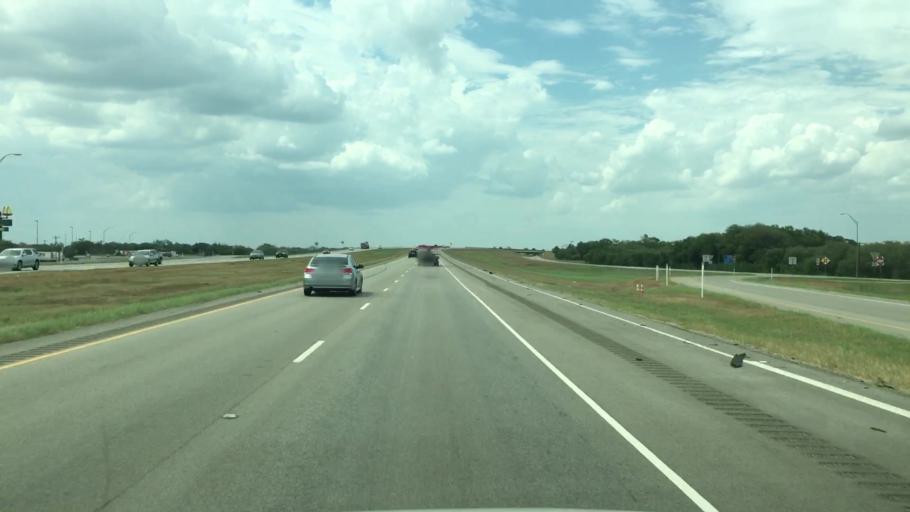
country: US
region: Texas
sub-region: Live Oak County
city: Three Rivers
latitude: 28.5204
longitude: -98.1805
